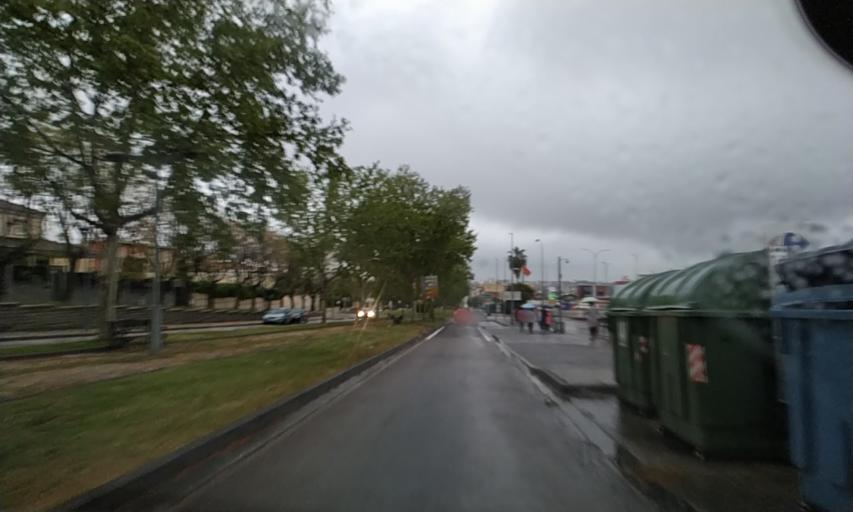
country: ES
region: Extremadura
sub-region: Provincia de Badajoz
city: Merida
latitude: 38.9062
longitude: -6.3622
